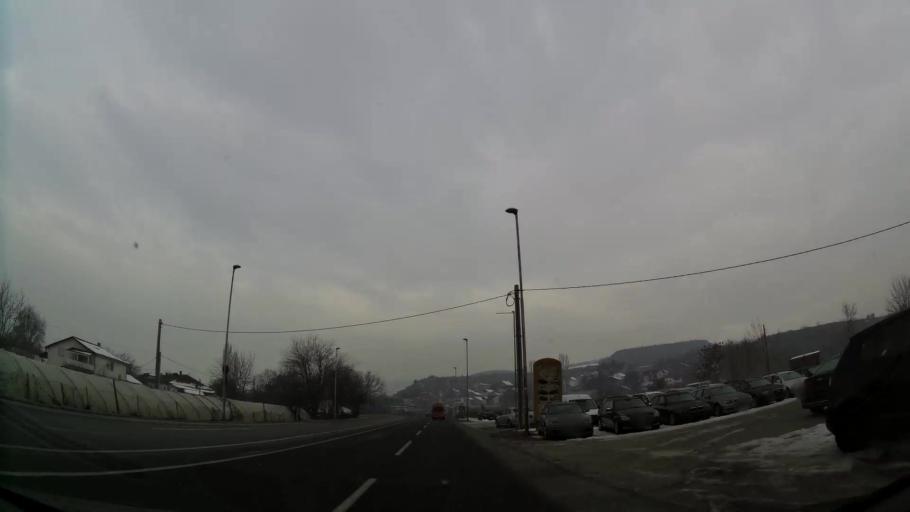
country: MK
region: Saraj
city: Saraj
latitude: 42.0075
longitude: 21.3298
